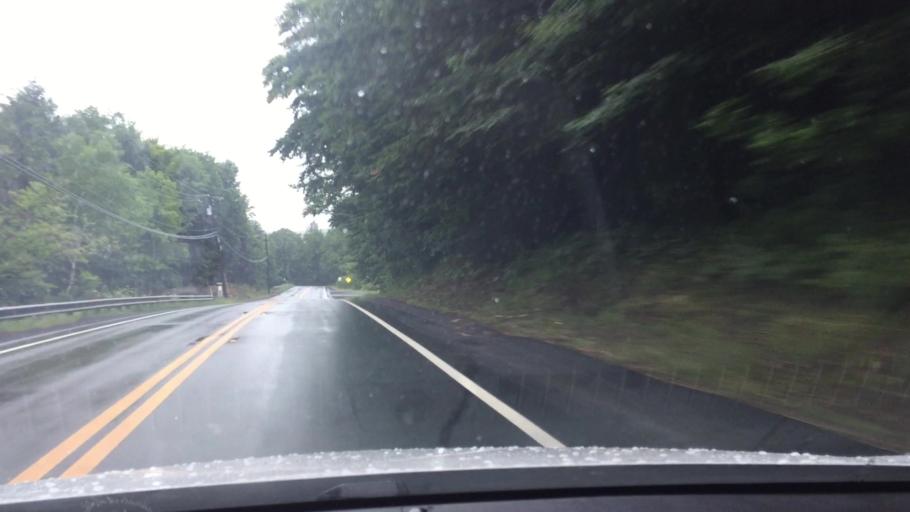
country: US
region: Massachusetts
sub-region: Berkshire County
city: Becket
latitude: 42.3080
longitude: -73.0738
